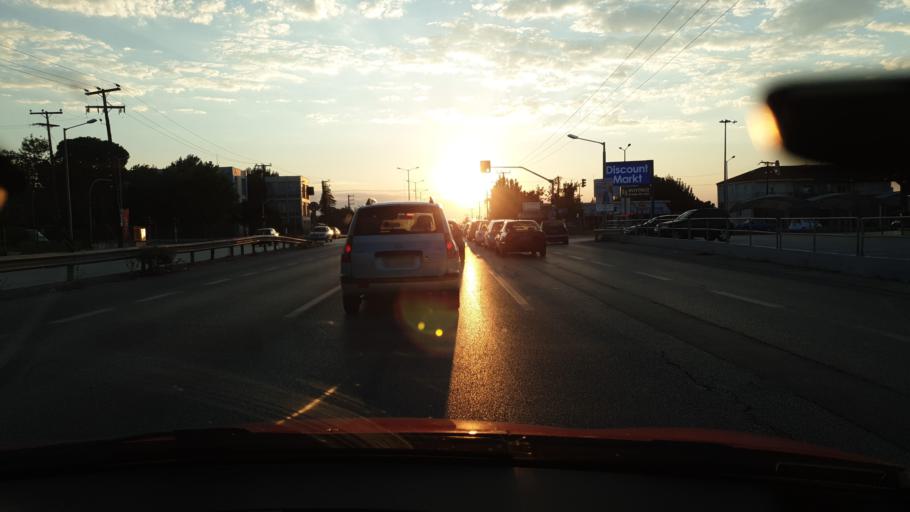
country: GR
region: Central Macedonia
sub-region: Nomos Thessalonikis
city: Peraia
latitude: 40.5005
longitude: 22.9513
